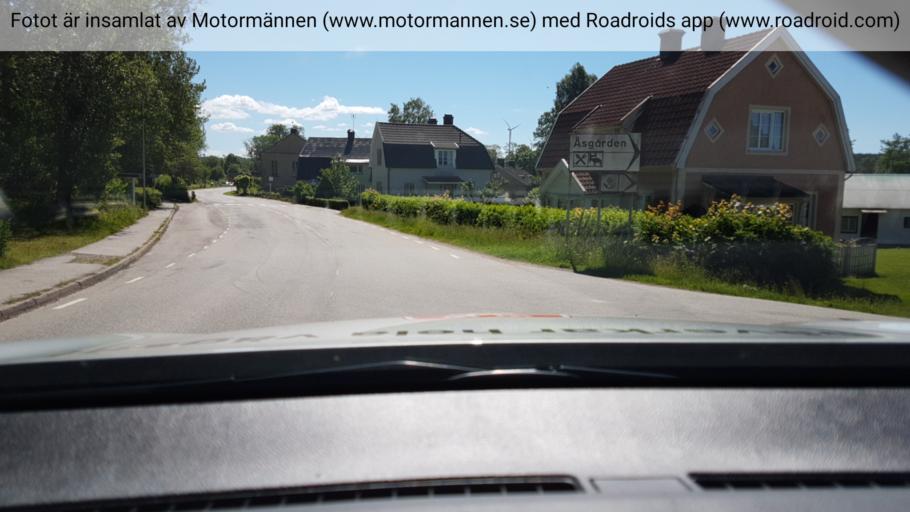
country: SE
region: Vaestra Goetaland
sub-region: Toreboda Kommun
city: Toereboda
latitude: 58.8038
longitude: 14.0605
